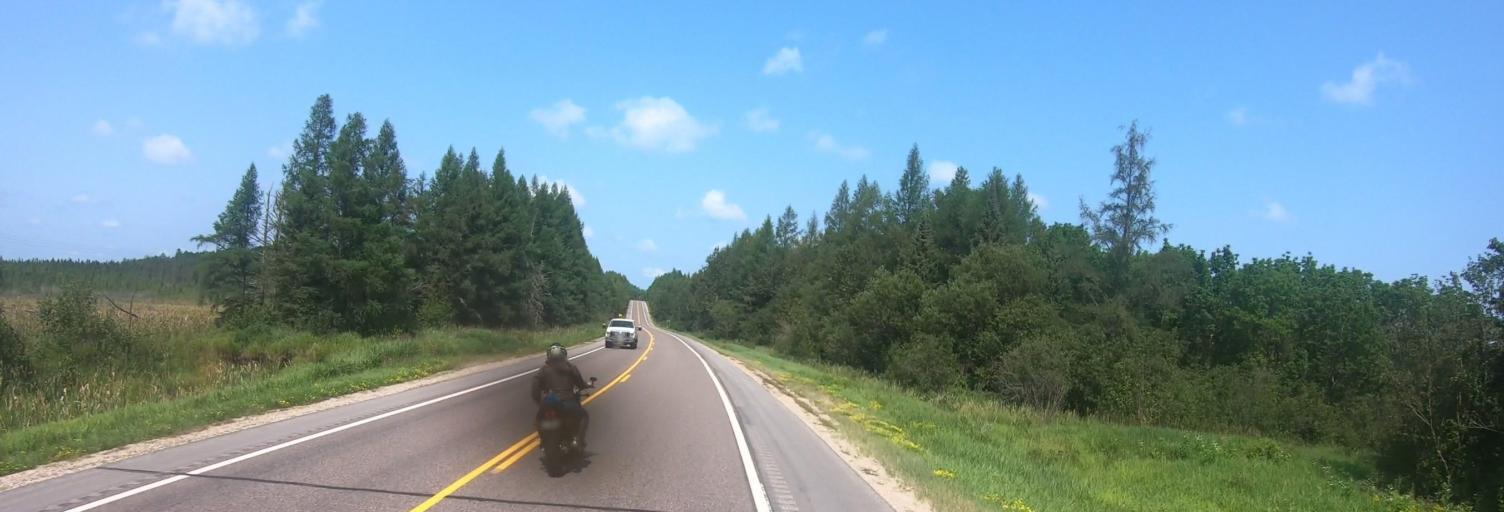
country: US
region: Minnesota
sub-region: Saint Louis County
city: Parkville
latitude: 48.1587
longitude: -92.5245
